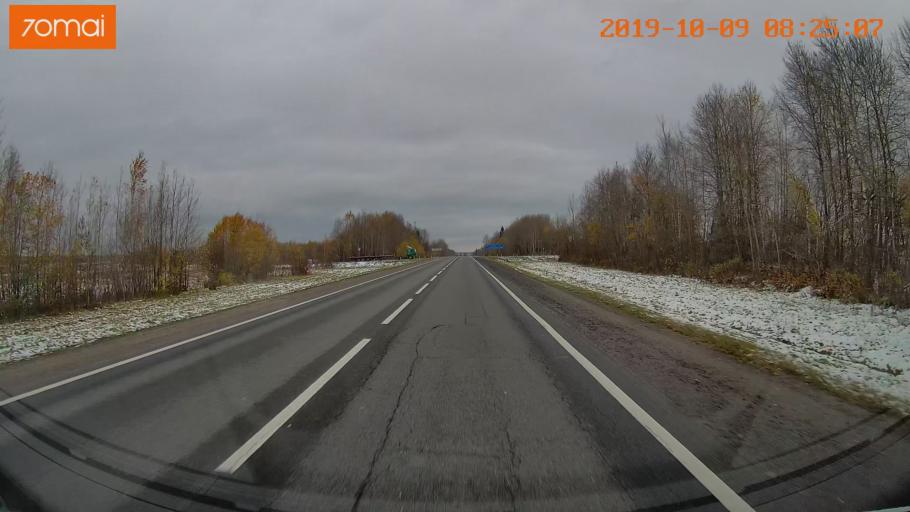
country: RU
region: Vologda
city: Gryazovets
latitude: 58.7762
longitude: 40.2743
